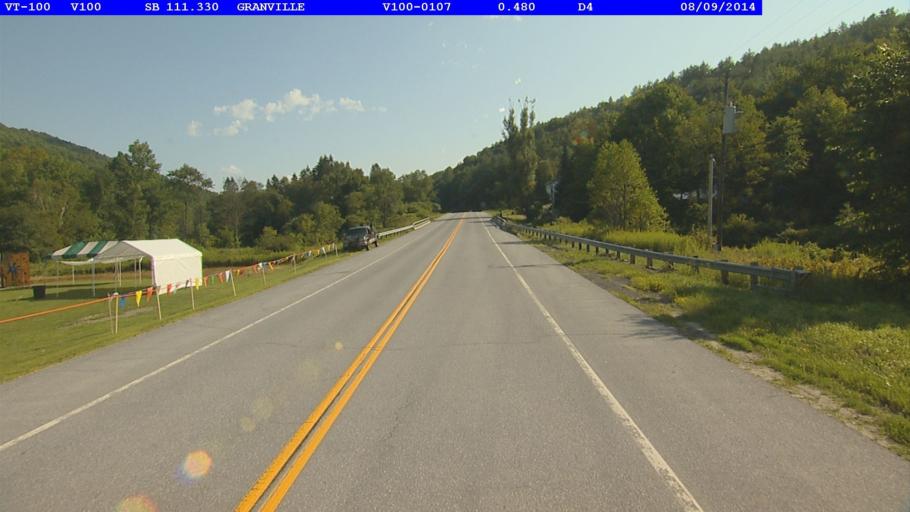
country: US
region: Vermont
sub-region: Orange County
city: Randolph
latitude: 43.9515
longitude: -72.8395
